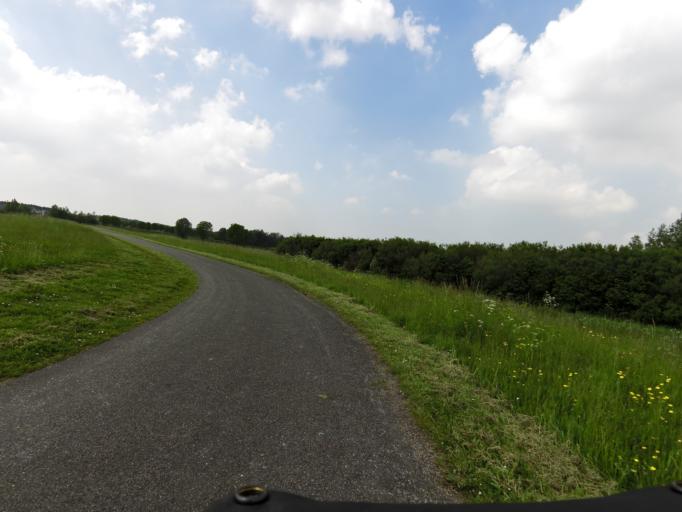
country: NL
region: South Holland
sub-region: Gemeente Spijkenisse
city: Spijkenisse
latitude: 51.8245
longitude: 4.2787
